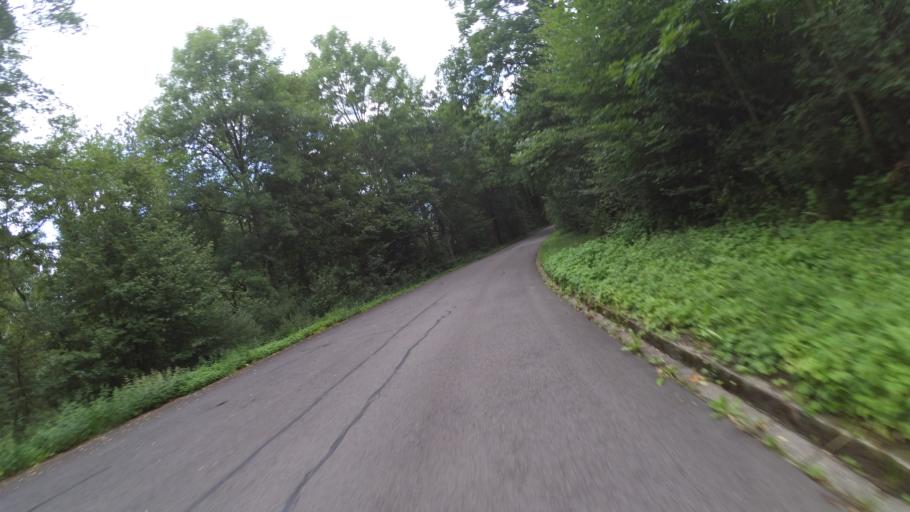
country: DE
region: Saarland
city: Nonnweiler
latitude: 49.5889
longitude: 6.9795
